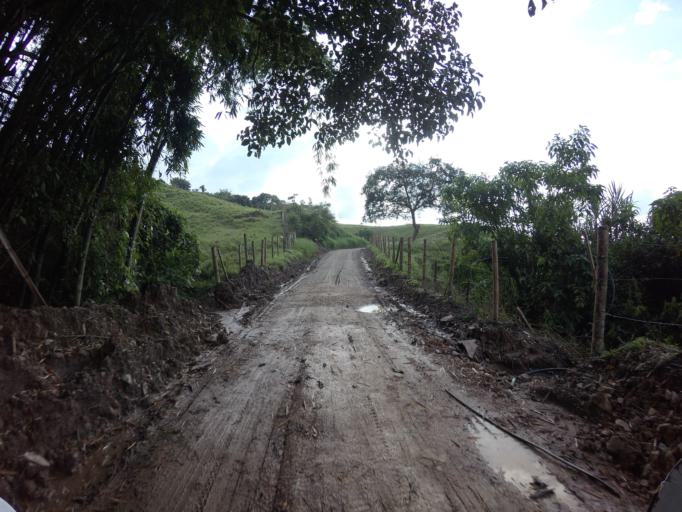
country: CO
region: Valle del Cauca
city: Ulloa
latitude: 4.7119
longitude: -75.7045
